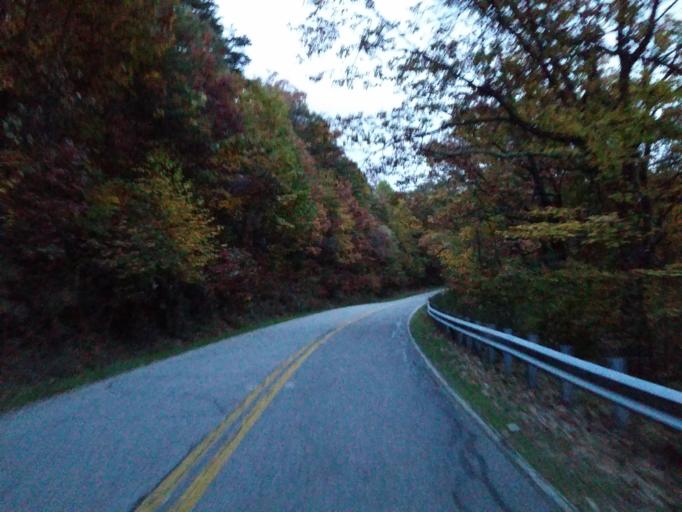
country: US
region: Georgia
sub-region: Lumpkin County
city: Dahlonega
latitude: 34.6666
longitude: -83.9848
